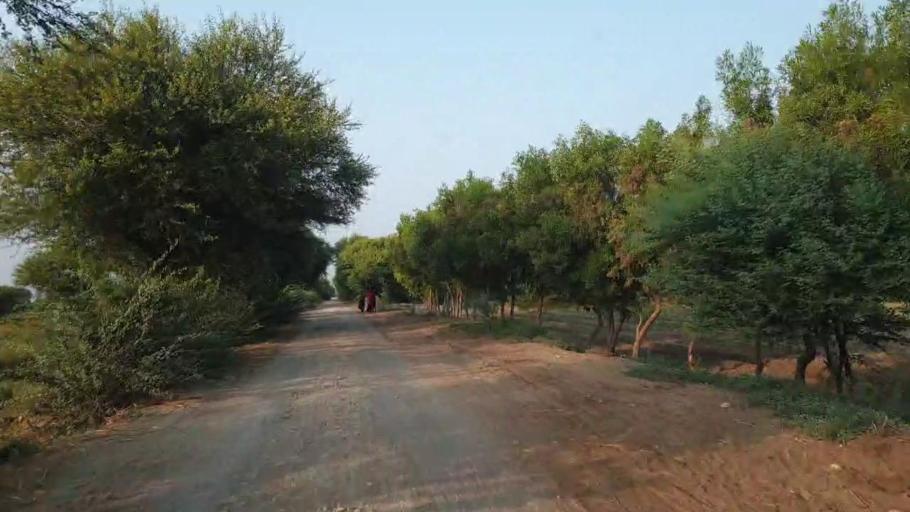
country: PK
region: Sindh
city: Rajo Khanani
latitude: 25.0432
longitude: 68.9644
